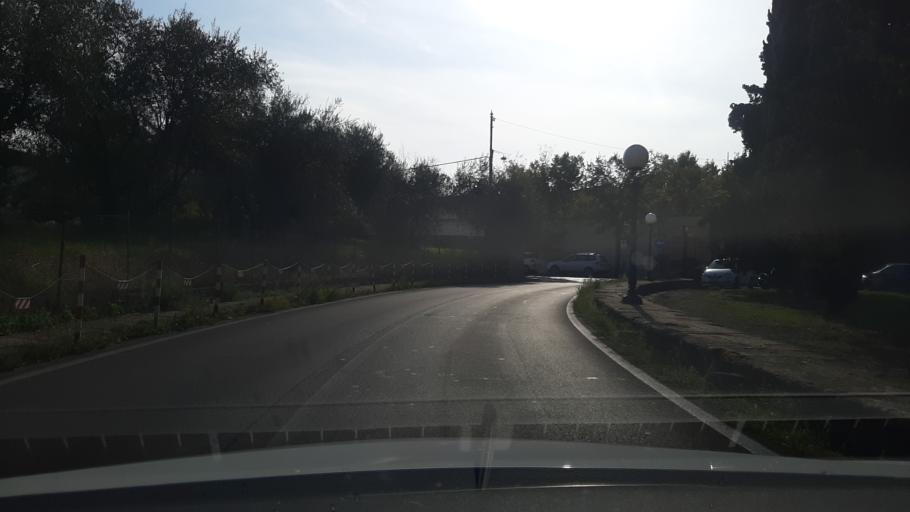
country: IT
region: Tuscany
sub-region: Province of Florence
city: Florence
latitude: 43.7502
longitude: 11.2478
